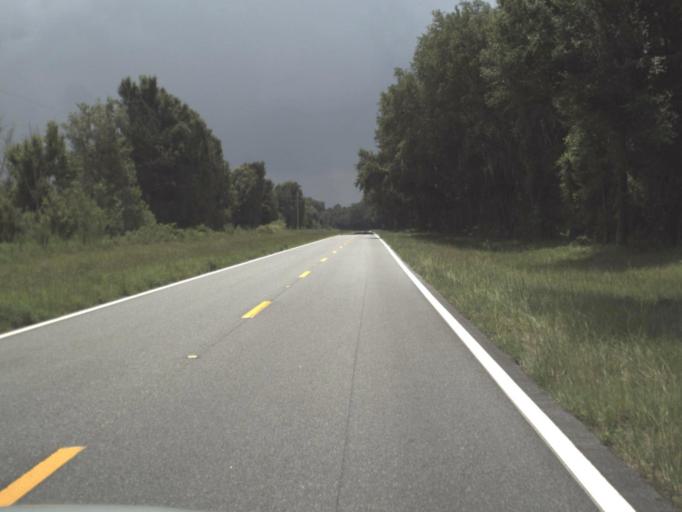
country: US
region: Florida
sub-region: Union County
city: Lake Butler
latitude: 29.8971
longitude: -82.3567
